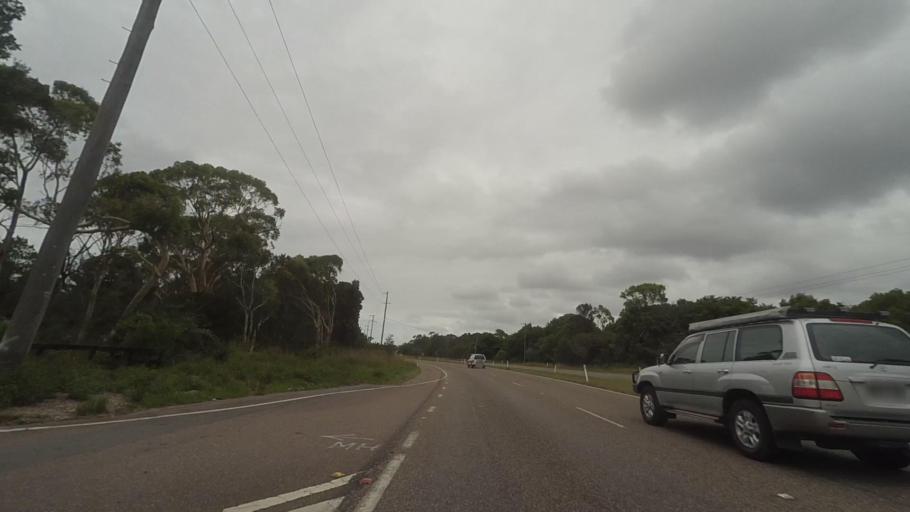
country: AU
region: New South Wales
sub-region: Wyong Shire
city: Buff Point
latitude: -33.1910
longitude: 151.5280
